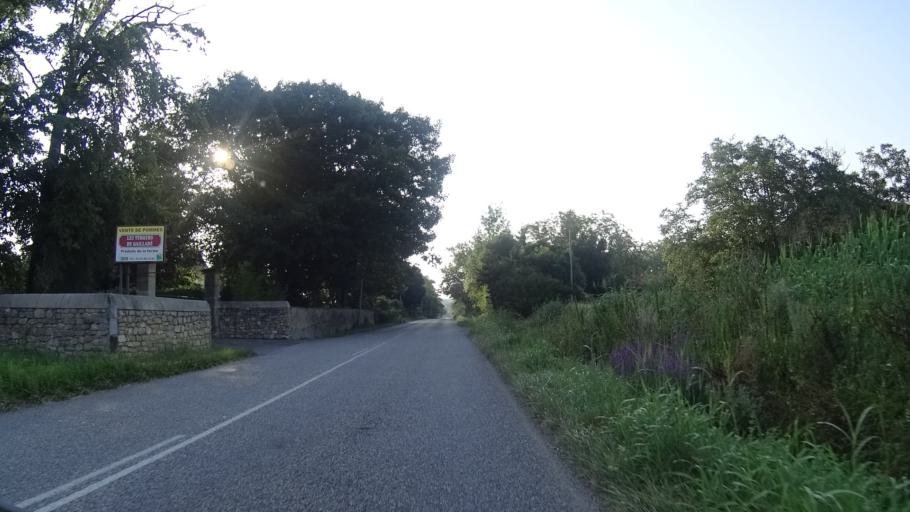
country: FR
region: Midi-Pyrenees
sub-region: Departement de l'Ariege
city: Mirepoix
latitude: 43.0845
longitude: 1.8976
